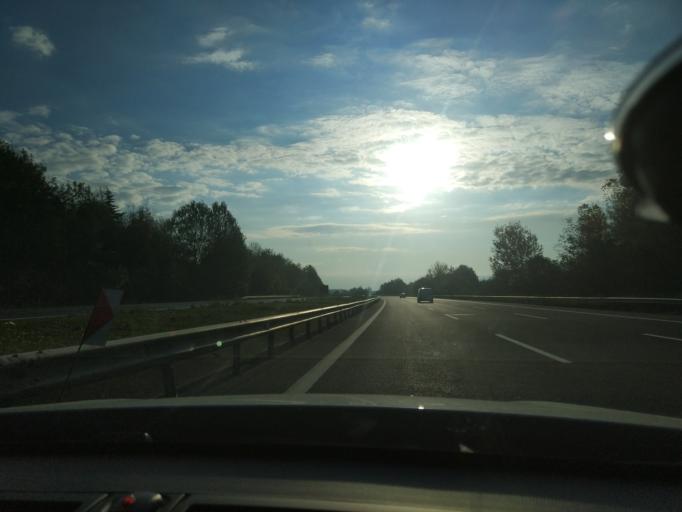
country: TR
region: Duzce
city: Duzce
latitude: 40.8055
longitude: 31.1552
